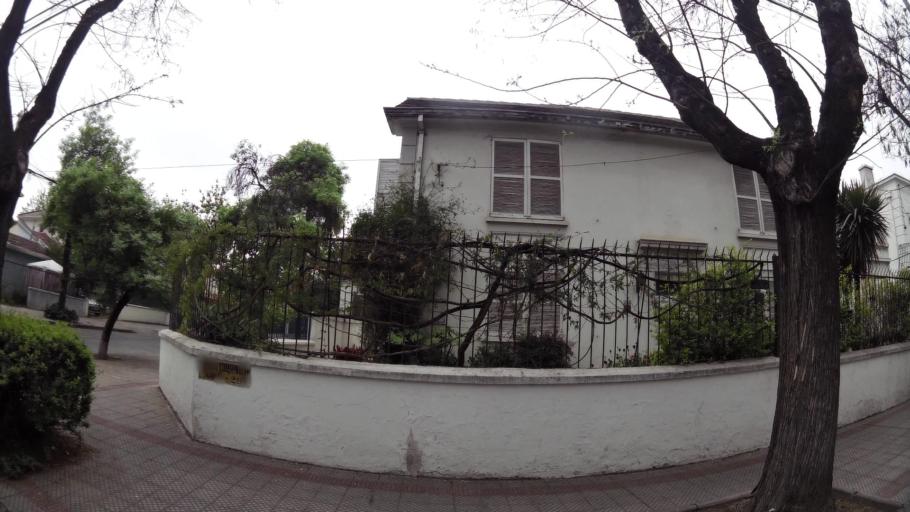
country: CL
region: Santiago Metropolitan
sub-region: Provincia de Santiago
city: Villa Presidente Frei, Nunoa, Santiago, Chile
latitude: -33.4350
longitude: -70.5910
